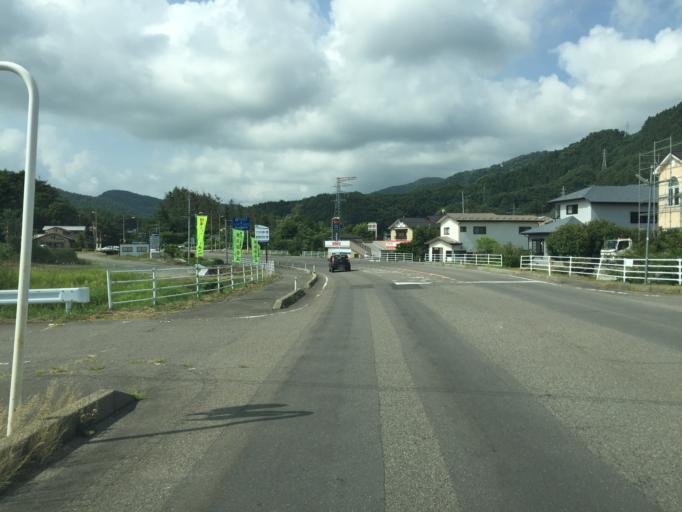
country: JP
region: Fukushima
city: Motomiya
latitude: 37.4900
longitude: 140.2782
